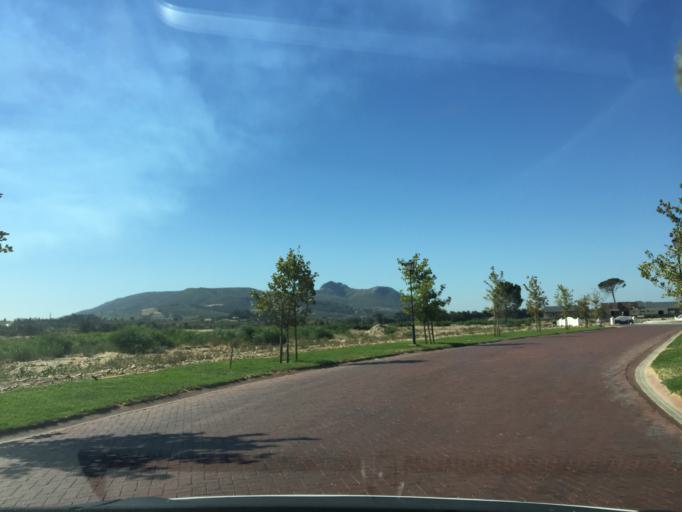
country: ZA
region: Western Cape
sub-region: Cape Winelands District Municipality
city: Paarl
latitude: -33.8101
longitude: 18.9613
